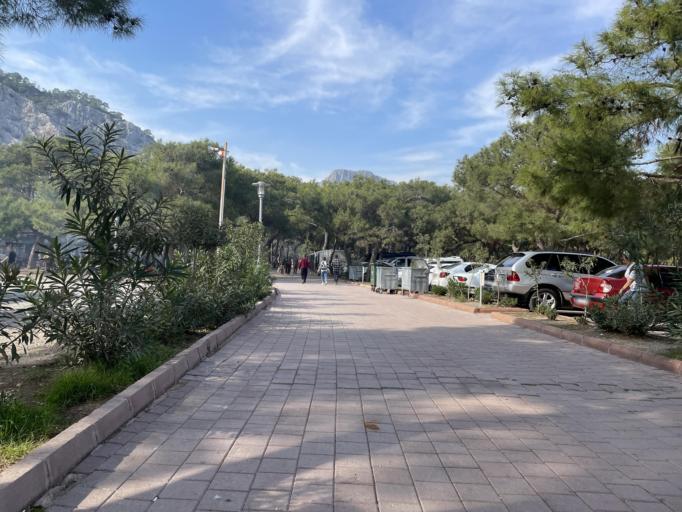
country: TR
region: Antalya
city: Cakirlar
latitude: 36.8288
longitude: 30.6006
